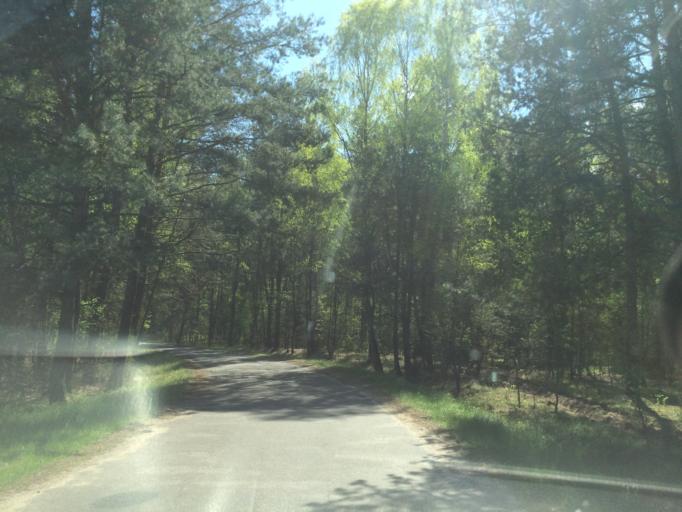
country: PL
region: Warmian-Masurian Voivodeship
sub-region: Powiat nowomiejski
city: Kurzetnik
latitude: 53.3749
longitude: 19.4917
